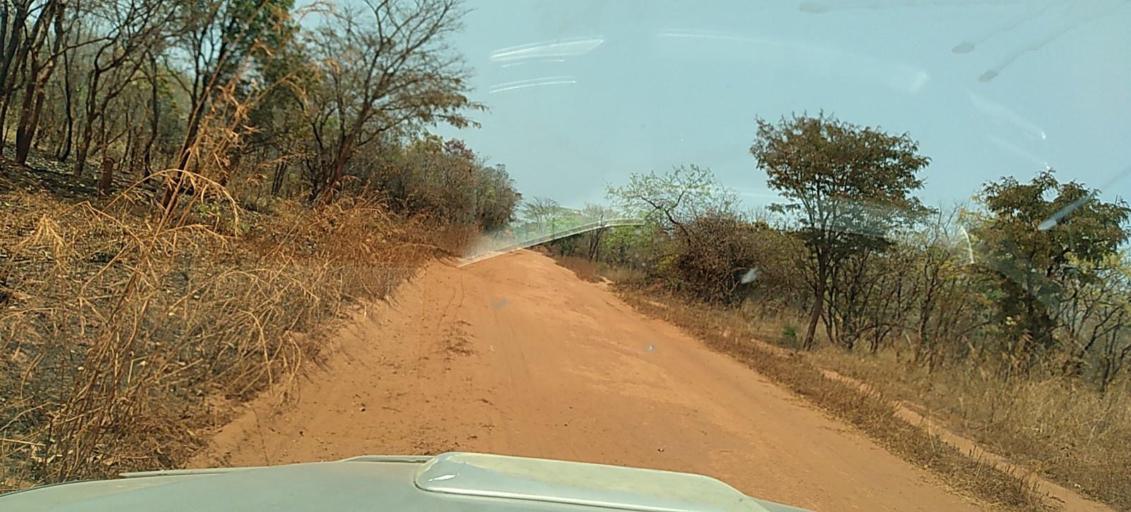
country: ZM
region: North-Western
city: Kasempa
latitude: -13.6240
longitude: 26.2102
